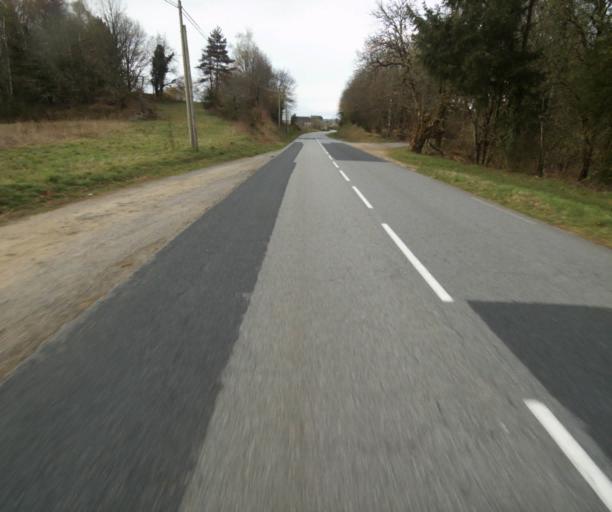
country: FR
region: Limousin
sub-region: Departement de la Correze
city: Correze
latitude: 45.3814
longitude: 1.8647
